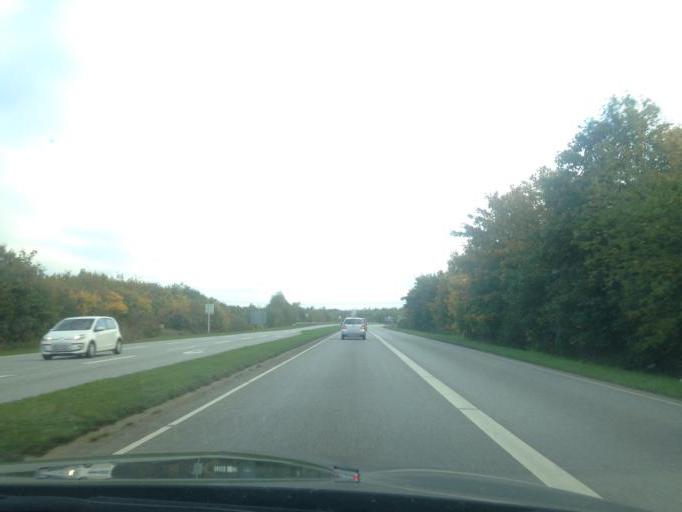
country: DK
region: South Denmark
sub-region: Kolding Kommune
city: Kolding
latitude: 55.5370
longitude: 9.4890
